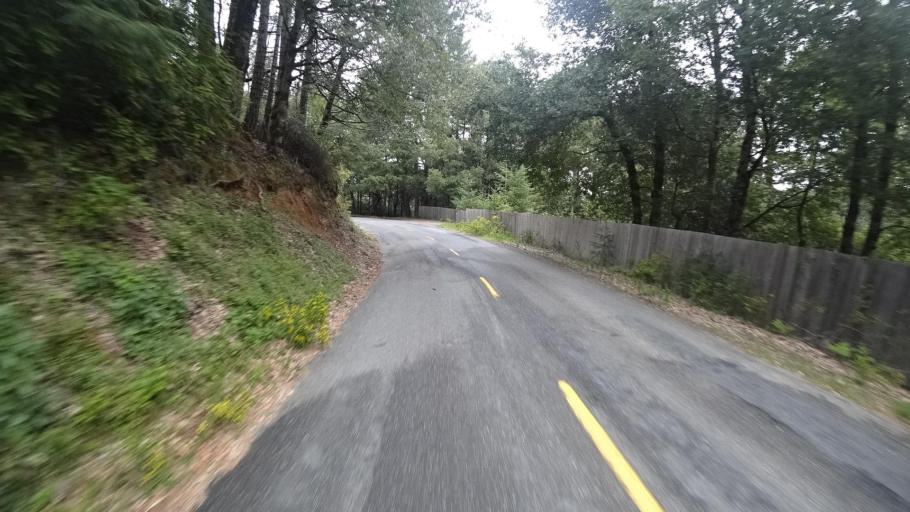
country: US
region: California
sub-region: Humboldt County
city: Redway
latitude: 40.2761
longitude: -123.7862
